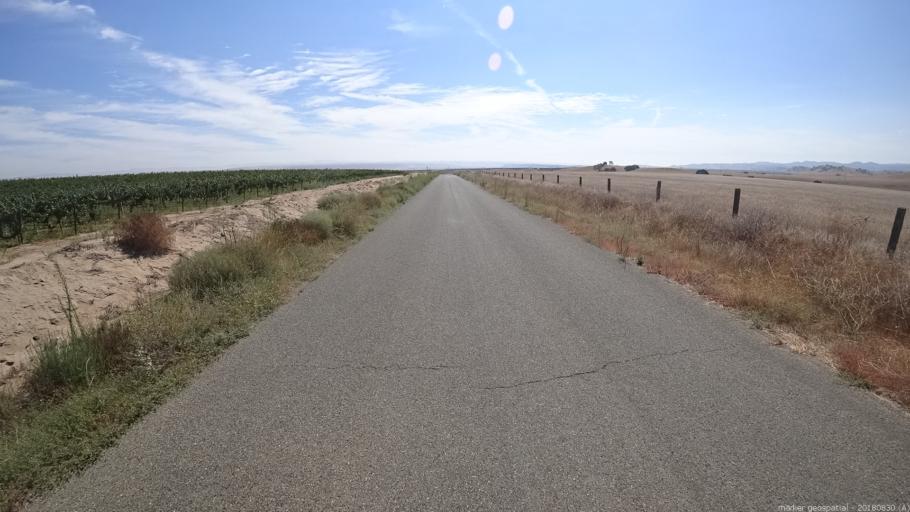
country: US
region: California
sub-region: Monterey County
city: King City
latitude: 36.1127
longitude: -121.0624
